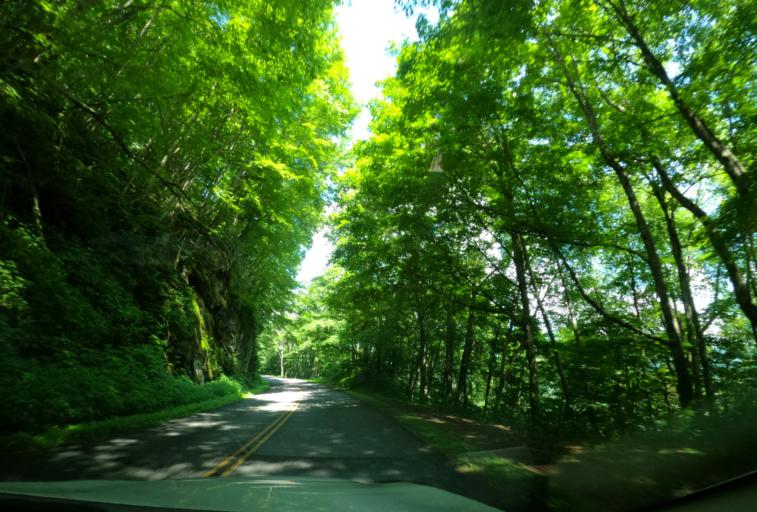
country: US
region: North Carolina
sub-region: Haywood County
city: Hazelwood
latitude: 35.4385
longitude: -83.0590
